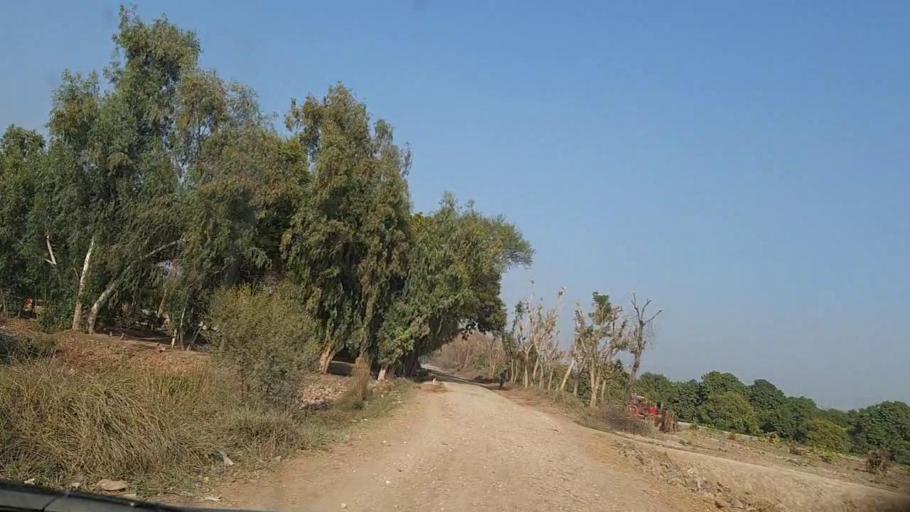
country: PK
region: Sindh
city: Moro
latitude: 26.7949
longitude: 67.9424
